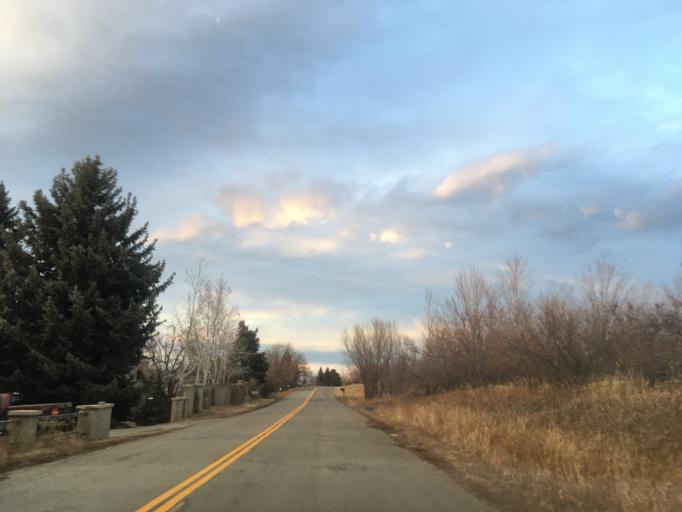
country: US
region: Colorado
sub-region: Boulder County
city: Superior
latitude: 39.9840
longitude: -105.1742
